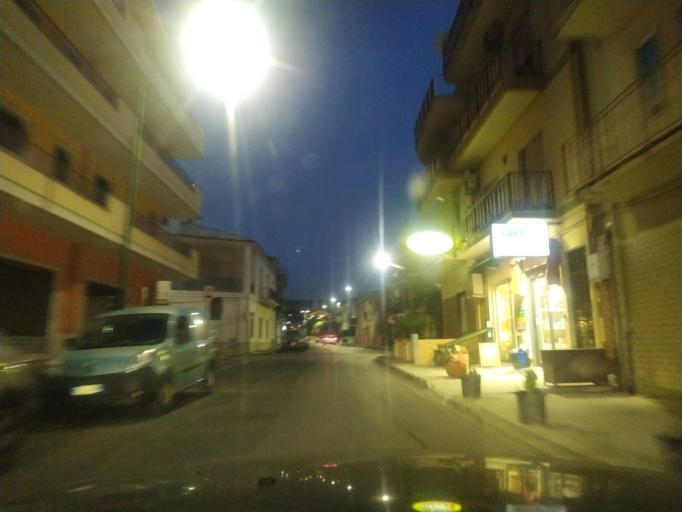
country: IT
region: Sicily
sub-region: Messina
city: Terme
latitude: 38.1382
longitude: 15.1619
